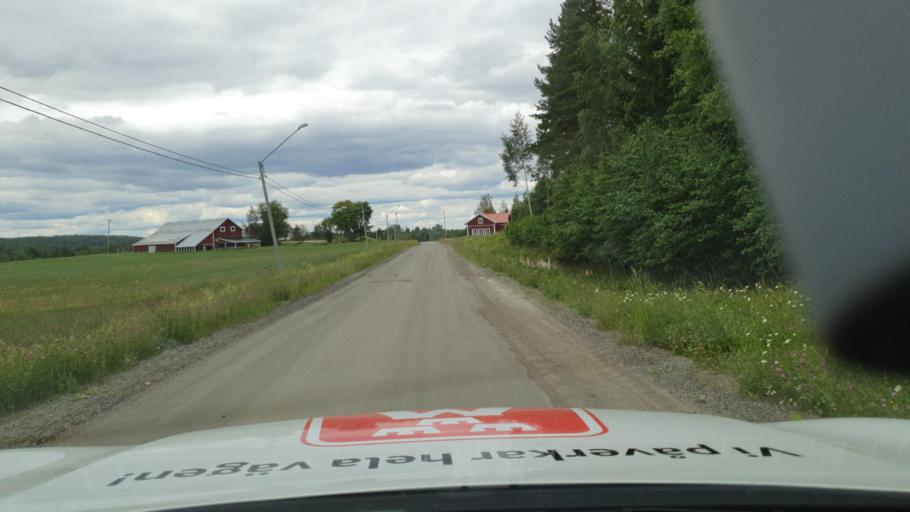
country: SE
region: Vaesterbotten
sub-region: Nordmalings Kommun
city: Nordmaling
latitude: 63.7195
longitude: 19.3229
